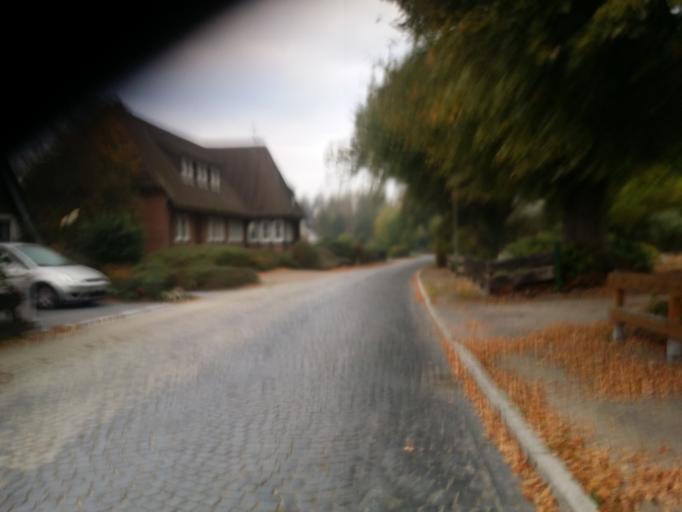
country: DE
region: Lower Saxony
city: Ritterhude
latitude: 53.1641
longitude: 8.7388
